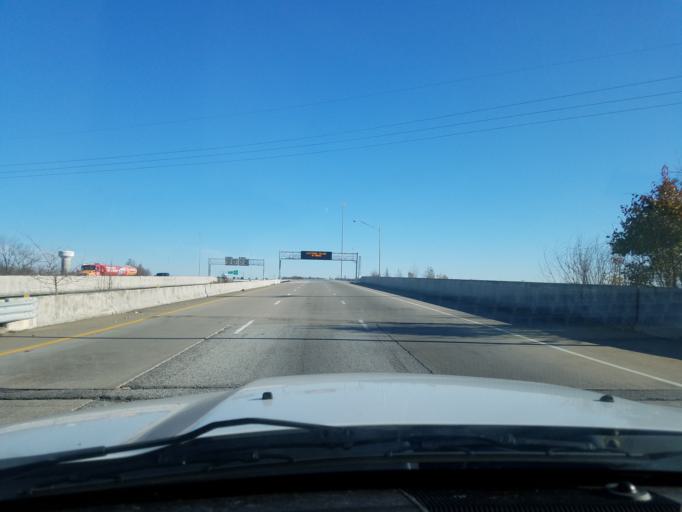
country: US
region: Indiana
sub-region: Clark County
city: Oak Park
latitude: 38.3453
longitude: -85.7194
